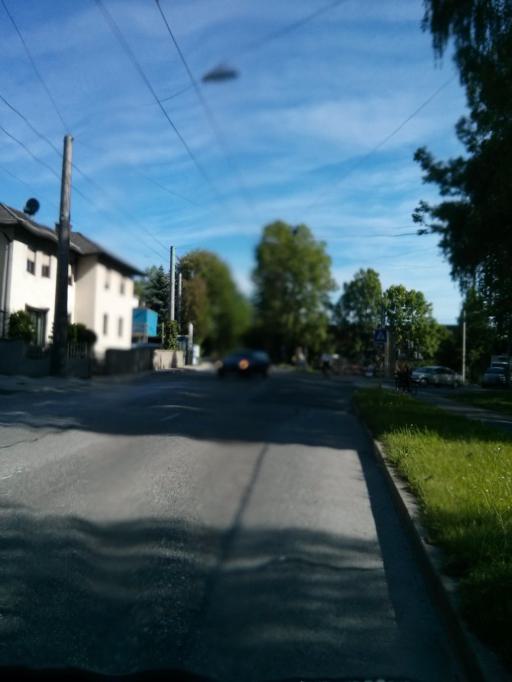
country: AT
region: Salzburg
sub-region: Salzburg Stadt
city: Salzburg
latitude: 47.8062
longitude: 13.0186
